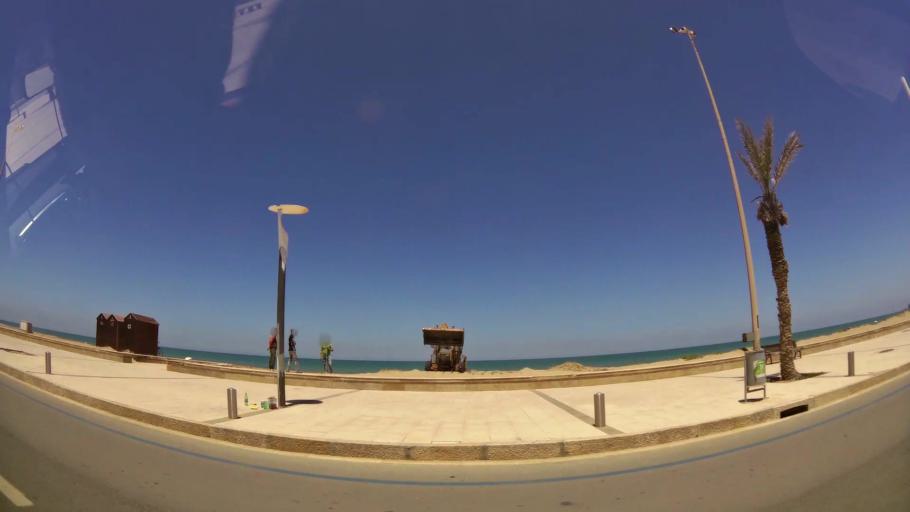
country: MA
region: Oriental
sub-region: Berkane-Taourirt
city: Madagh
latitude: 35.0850
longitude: -2.2176
